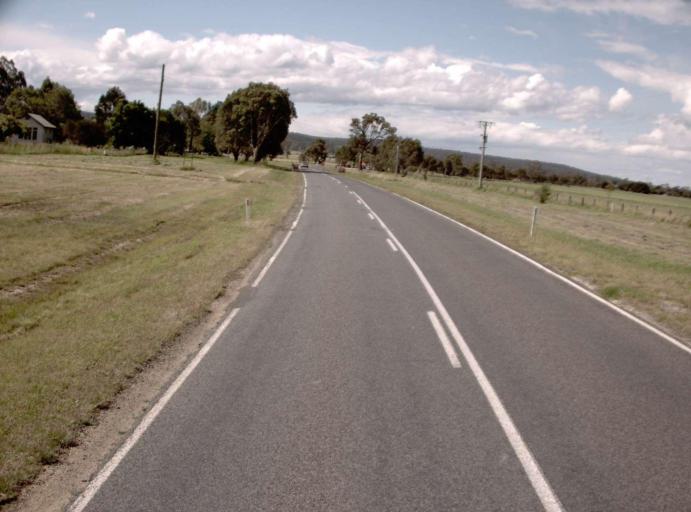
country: AU
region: Victoria
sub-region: Latrobe
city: Traralgon
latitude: -38.1501
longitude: 146.5229
